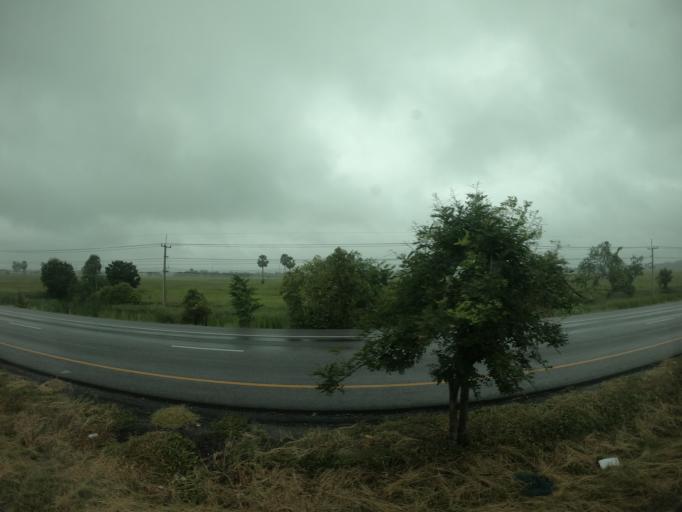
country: TH
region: Nakhon Ratchasima
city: Phimai
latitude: 15.3026
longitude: 102.4216
